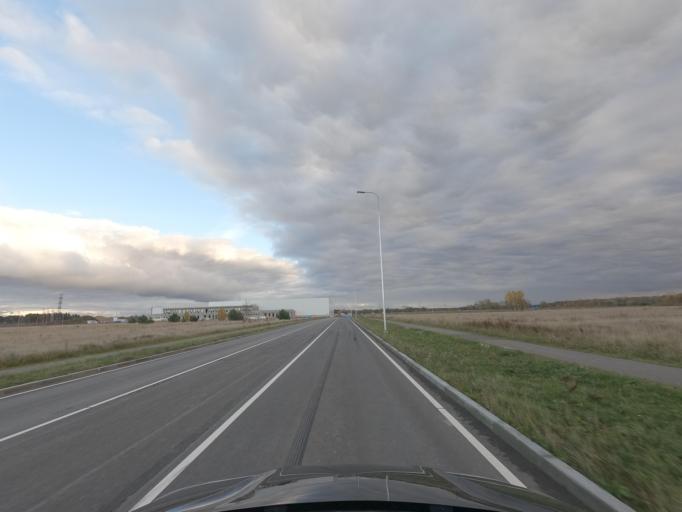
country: EE
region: Harju
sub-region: Saue vald
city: Laagri
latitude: 59.3353
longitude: 24.5956
